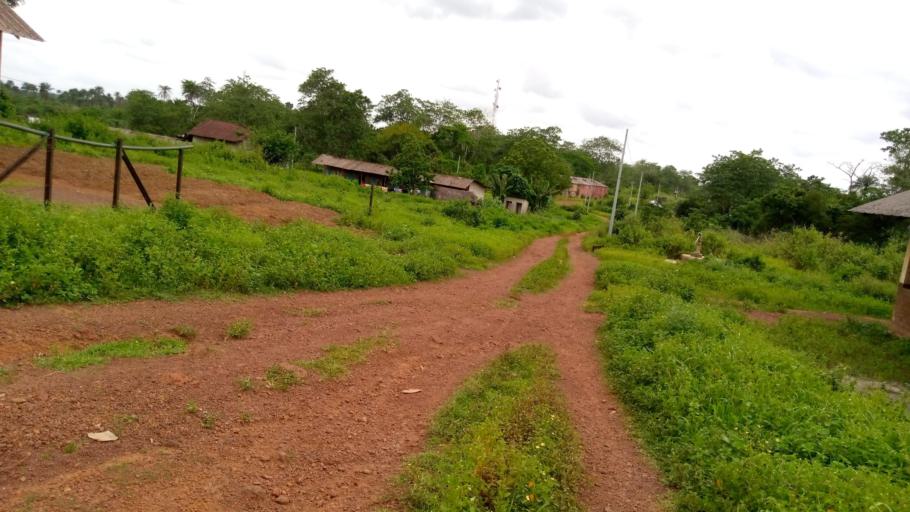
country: SL
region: Southern Province
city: Rotifunk
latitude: 8.1919
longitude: -12.5675
